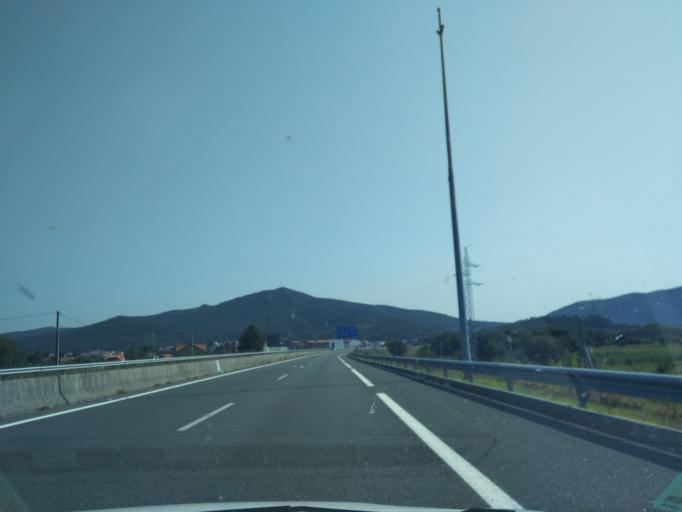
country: ES
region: Galicia
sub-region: Provincia da Coruna
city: Padron
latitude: 42.7282
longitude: -8.6688
